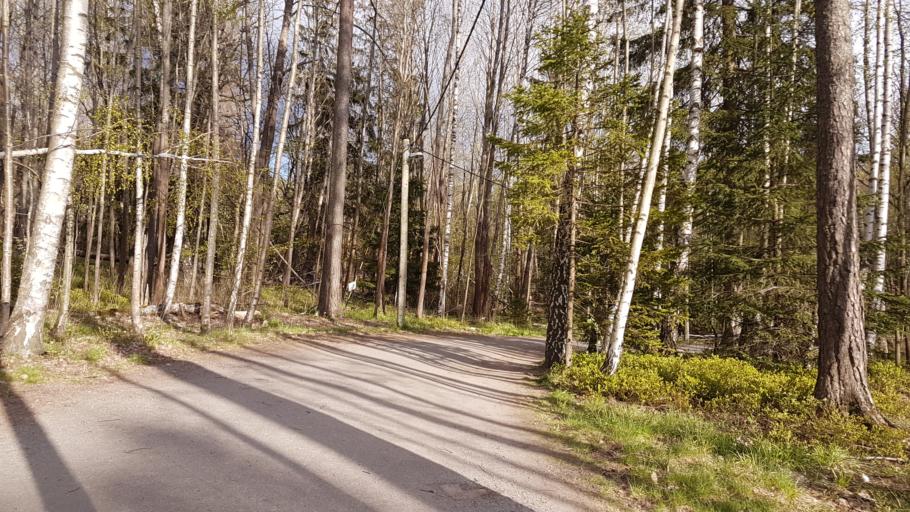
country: SE
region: Stockholm
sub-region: Nacka Kommun
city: Nacka
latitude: 59.2866
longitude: 18.1259
